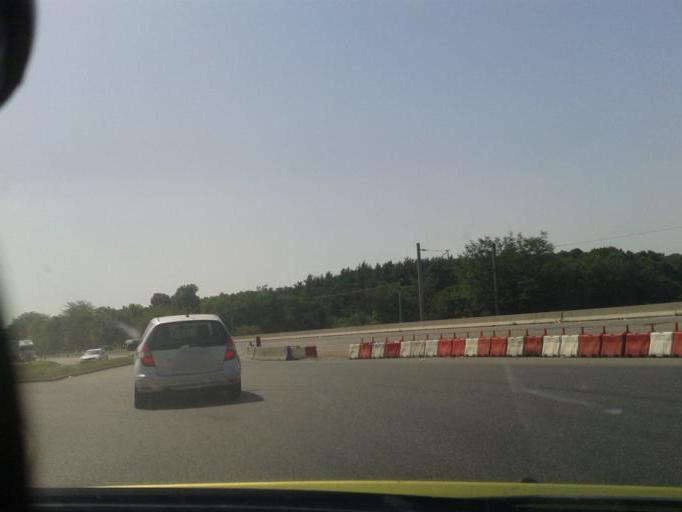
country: RO
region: Ilfov
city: Stefanestii de Jos
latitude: 44.5212
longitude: 26.1751
